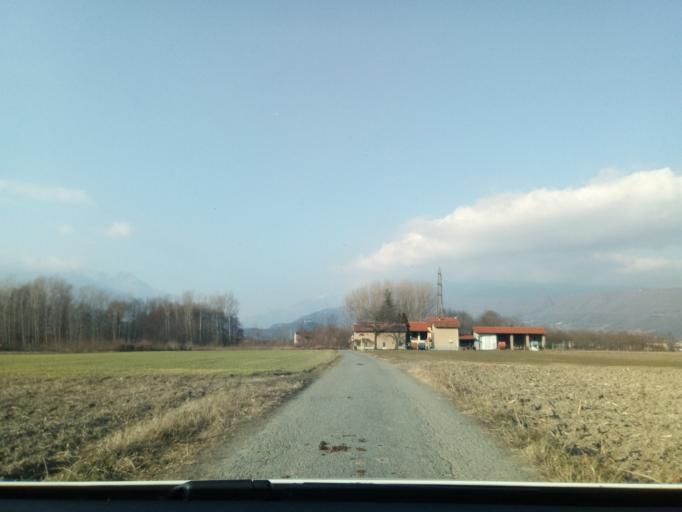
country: IT
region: Piedmont
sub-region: Provincia di Torino
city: Bollengo
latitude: 45.4578
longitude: 7.9207
